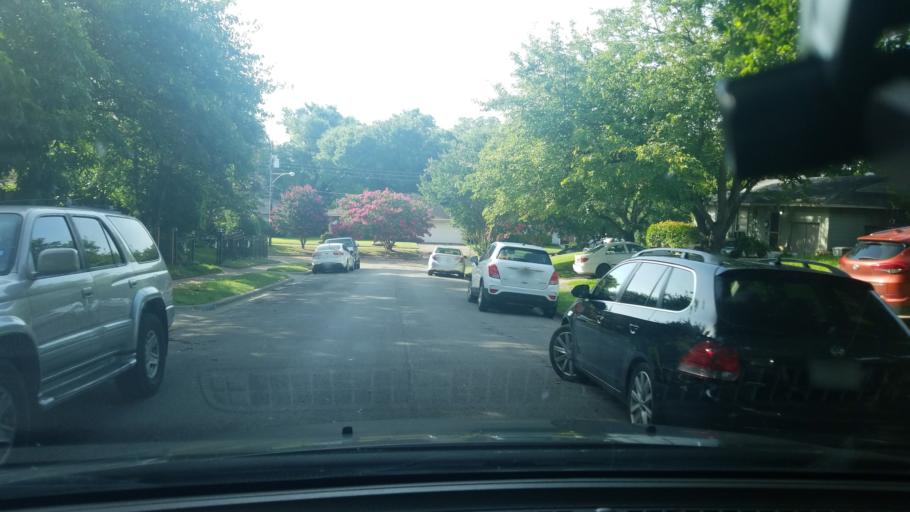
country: US
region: Texas
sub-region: Dallas County
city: Highland Park
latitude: 32.7987
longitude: -96.7135
